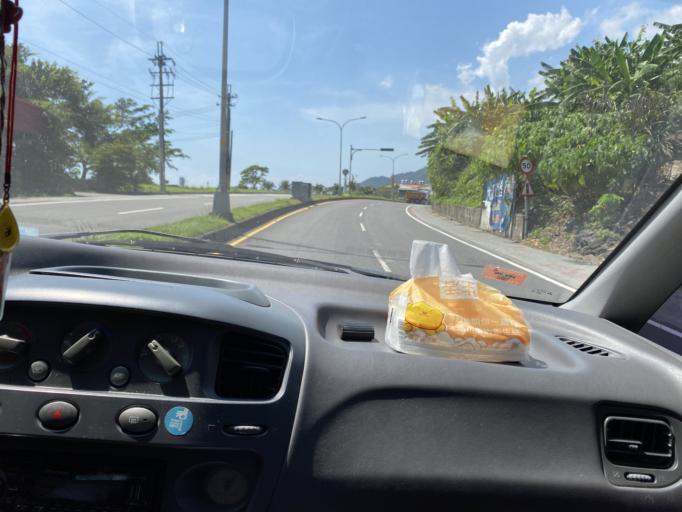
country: TW
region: Taiwan
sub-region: Yilan
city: Yilan
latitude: 24.9427
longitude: 121.9022
